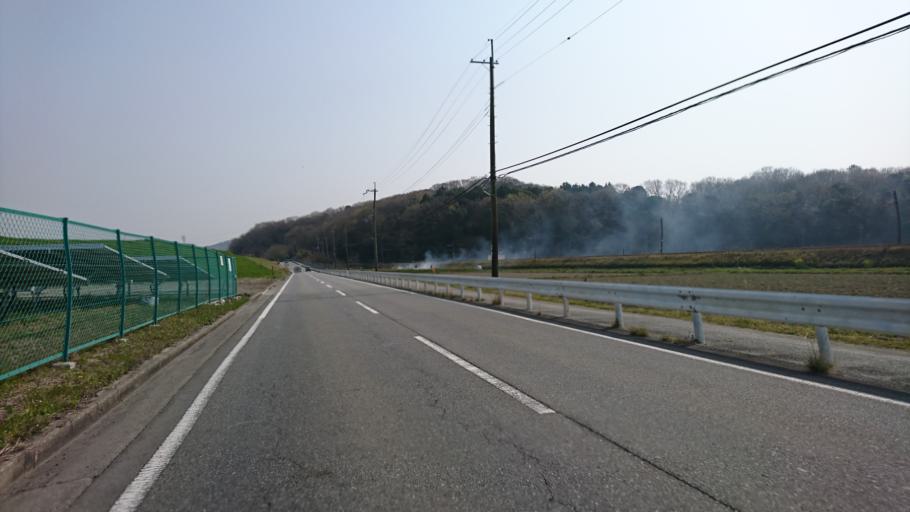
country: JP
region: Hyogo
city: Ono
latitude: 34.8488
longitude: 134.9099
